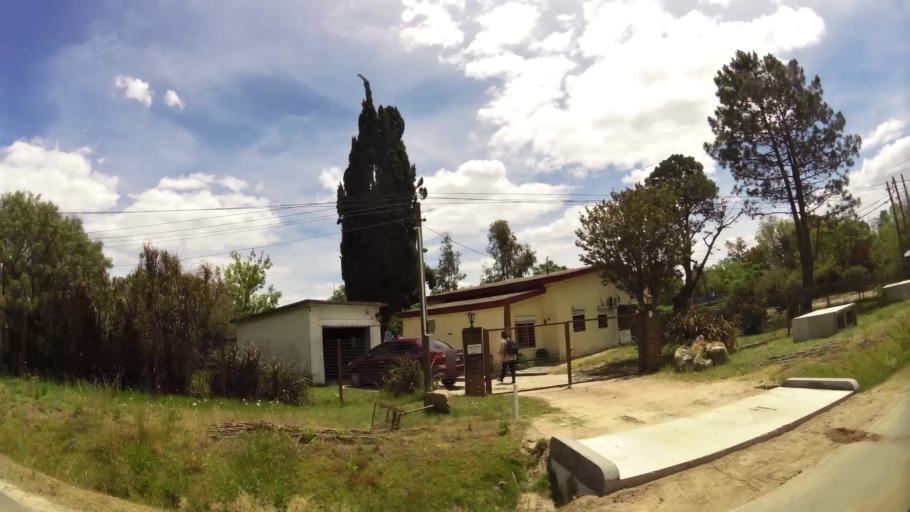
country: UY
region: Canelones
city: Colonia Nicolich
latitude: -34.8223
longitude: -55.9693
